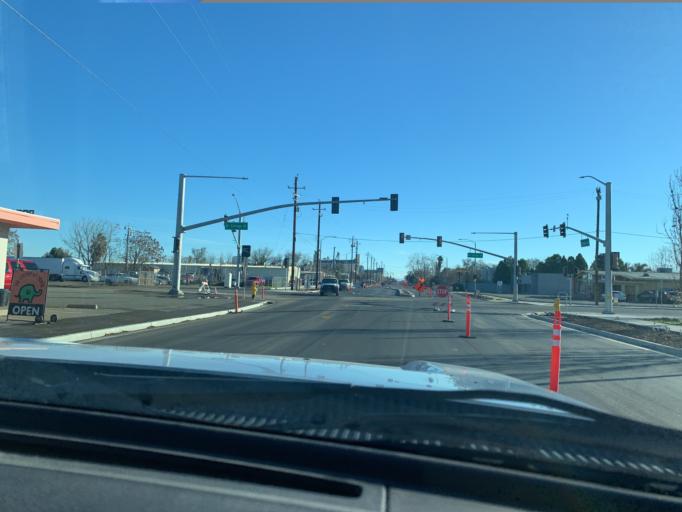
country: US
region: California
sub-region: Yolo County
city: Woodland
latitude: 38.6919
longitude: -121.7754
